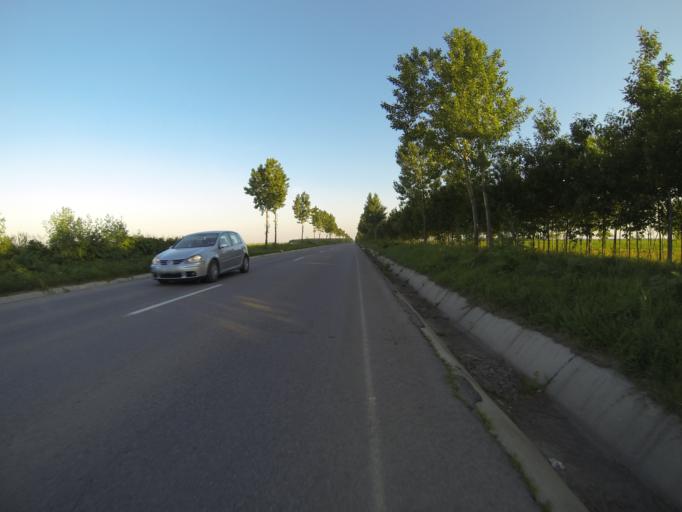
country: RO
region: Dolj
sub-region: Comuna Segarcea
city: Segarcea
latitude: 44.1332
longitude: 23.7390
